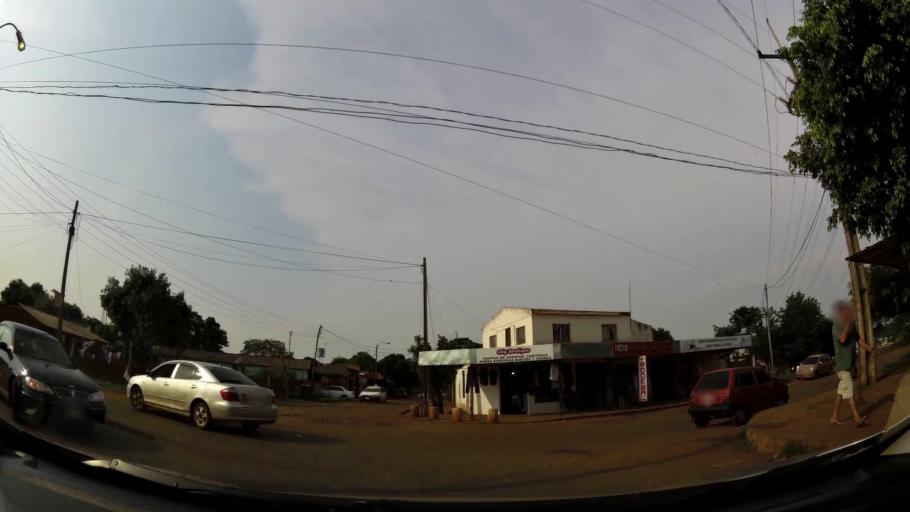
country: PY
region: Alto Parana
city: Ciudad del Este
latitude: -25.4836
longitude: -54.6658
